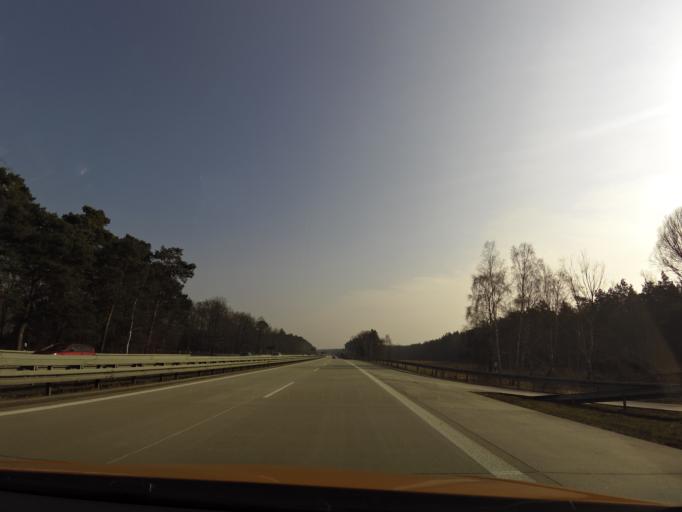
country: DE
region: Brandenburg
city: Briesen
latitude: 52.3280
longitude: 14.2720
